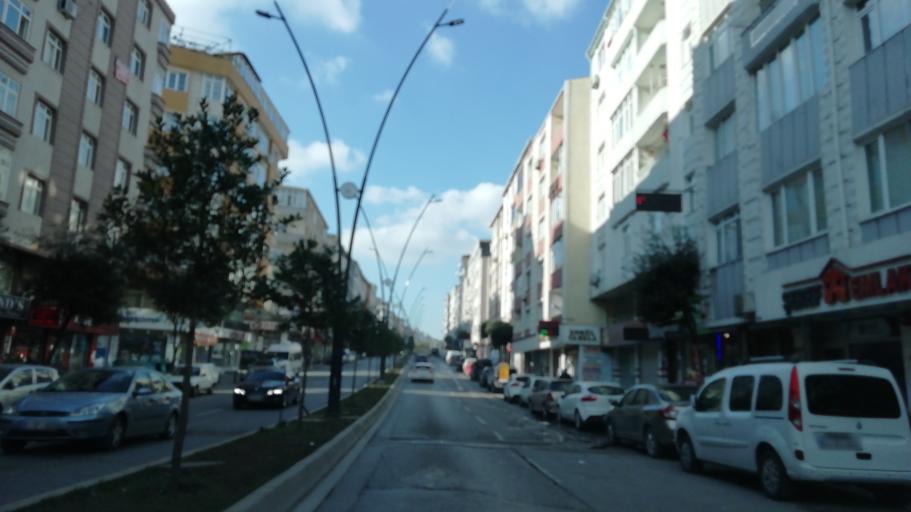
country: TR
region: Istanbul
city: Esenler
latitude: 41.0580
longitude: 28.9247
